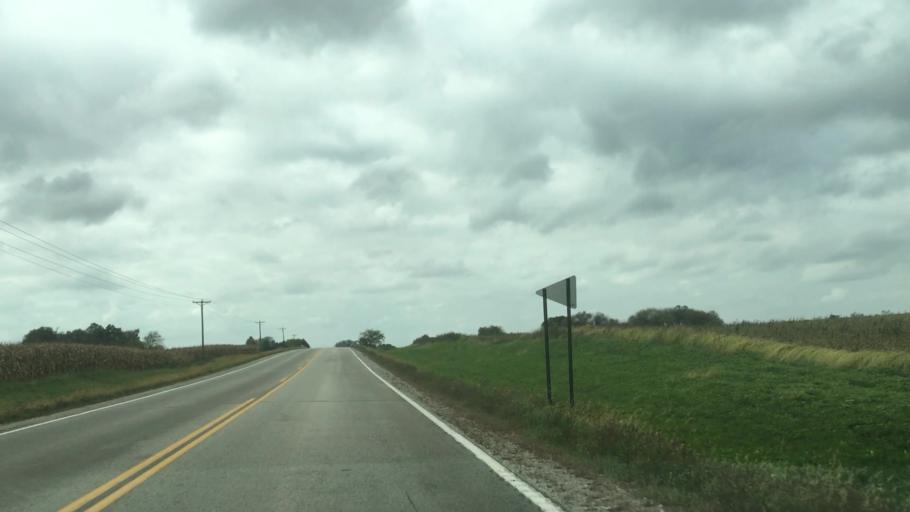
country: US
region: Minnesota
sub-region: Fillmore County
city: Preston
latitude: 43.7353
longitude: -92.1065
